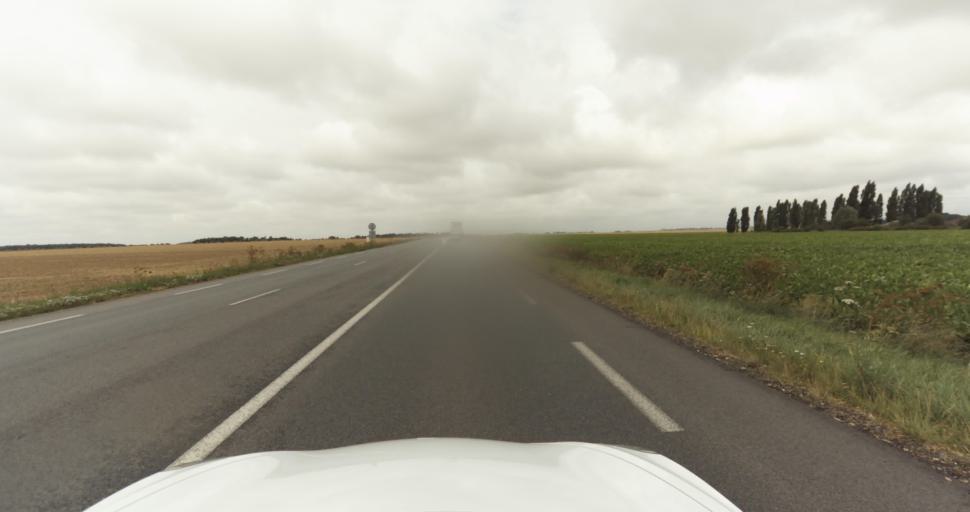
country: FR
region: Haute-Normandie
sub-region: Departement de l'Eure
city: Saint-Sebastien-de-Morsent
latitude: 49.0428
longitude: 1.0780
